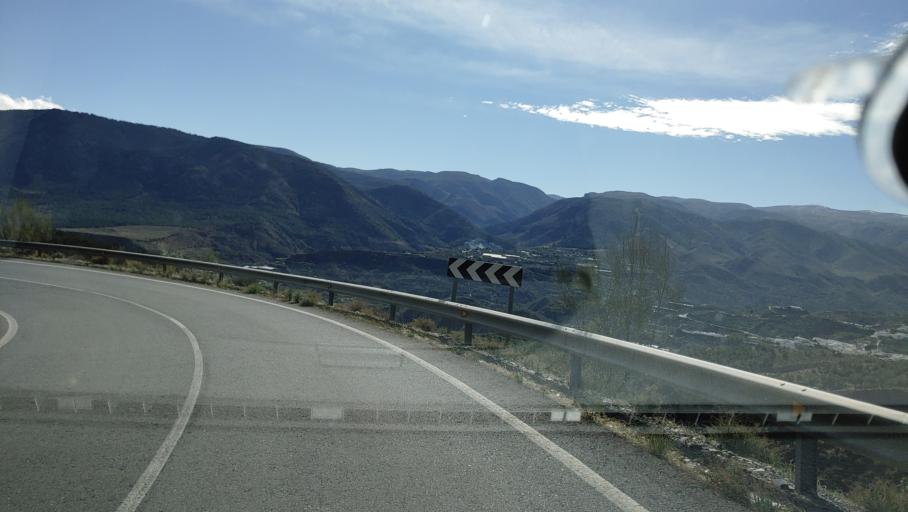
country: ES
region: Andalusia
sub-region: Provincia de Almeria
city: Canjayar
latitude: 37.0201
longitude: -2.7267
